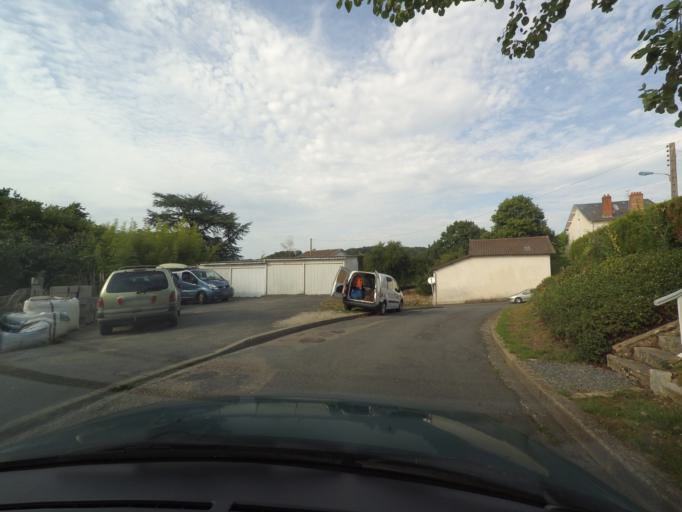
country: FR
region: Limousin
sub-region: Departement de la Haute-Vienne
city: Aixe-sur-Vienne
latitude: 45.7970
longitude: 1.1295
